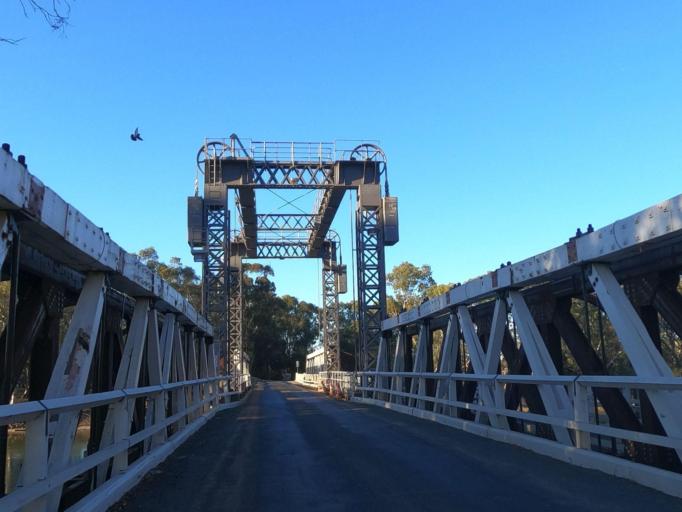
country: AU
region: Victoria
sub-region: Swan Hill
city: Swan Hill
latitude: -35.3380
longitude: 143.5624
